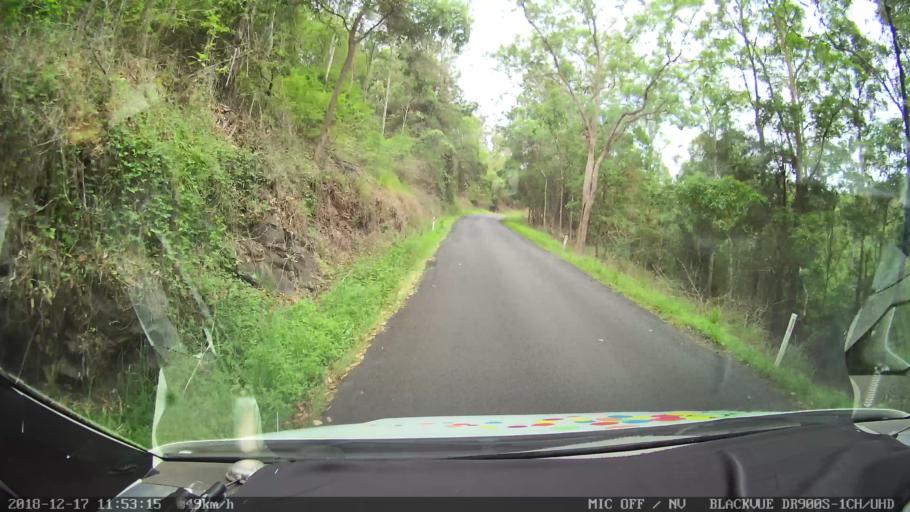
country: AU
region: New South Wales
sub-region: Kyogle
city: Kyogle
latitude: -28.5756
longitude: 152.5870
